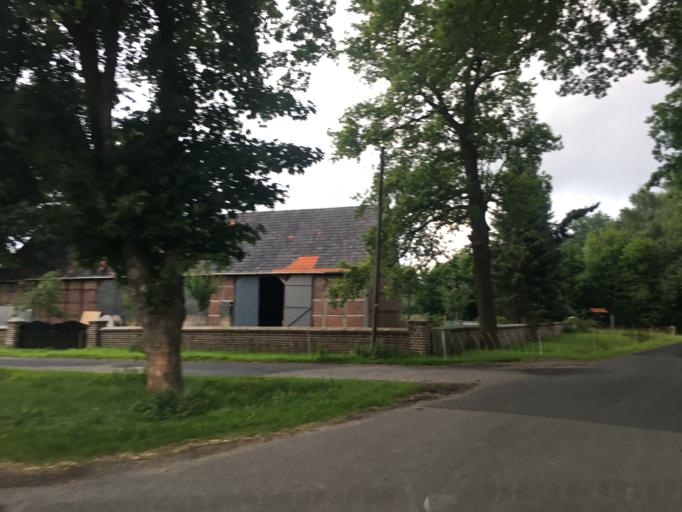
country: DE
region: North Rhine-Westphalia
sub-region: Regierungsbezirk Munster
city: Greven
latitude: 52.0510
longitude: 7.6044
